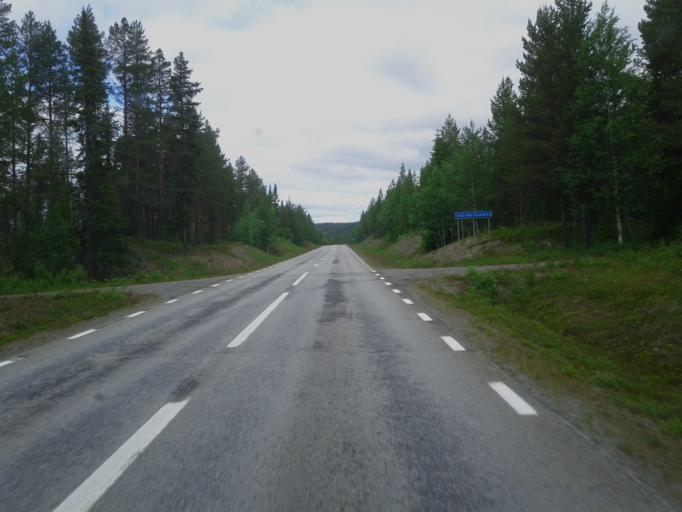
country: SE
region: Vaesterbotten
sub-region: Storumans Kommun
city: Fristad
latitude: 65.3700
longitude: 16.5187
